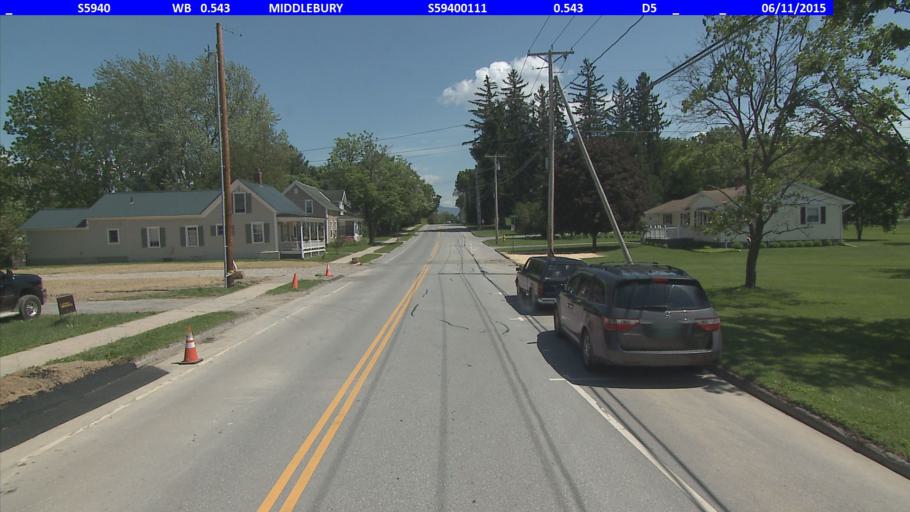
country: US
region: Vermont
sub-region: Addison County
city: Middlebury (village)
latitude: 44.0172
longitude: -73.1788
